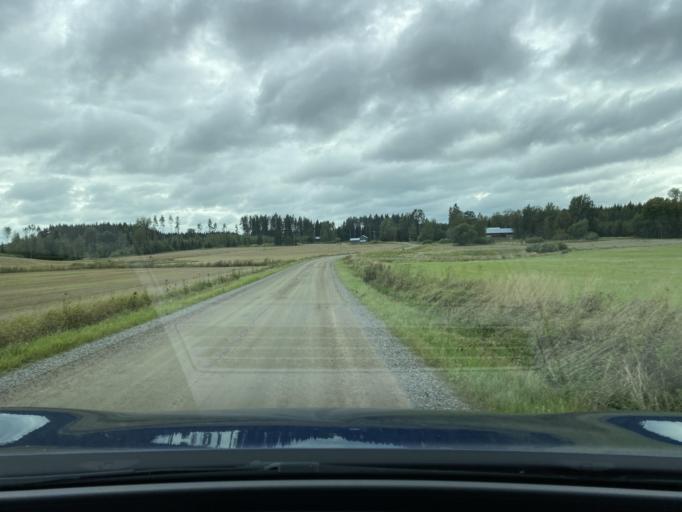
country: FI
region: Pirkanmaa
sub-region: Lounais-Pirkanmaa
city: Punkalaidun
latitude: 61.1832
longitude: 23.1849
